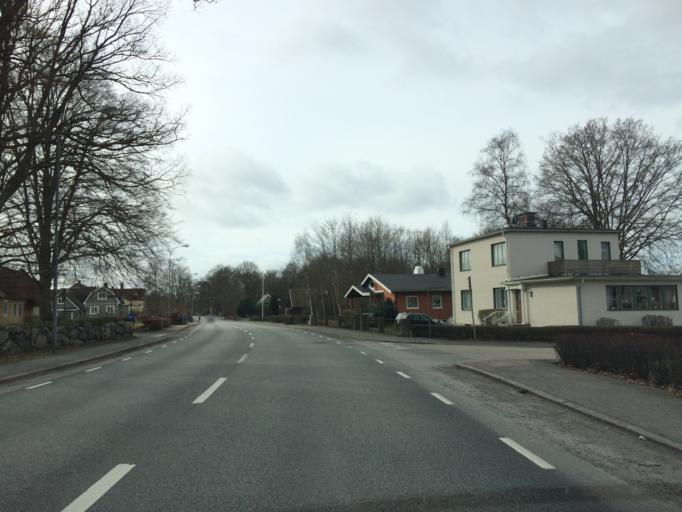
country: SE
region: Skane
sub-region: Osby Kommun
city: Lonsboda
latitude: 56.3965
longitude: 14.3172
